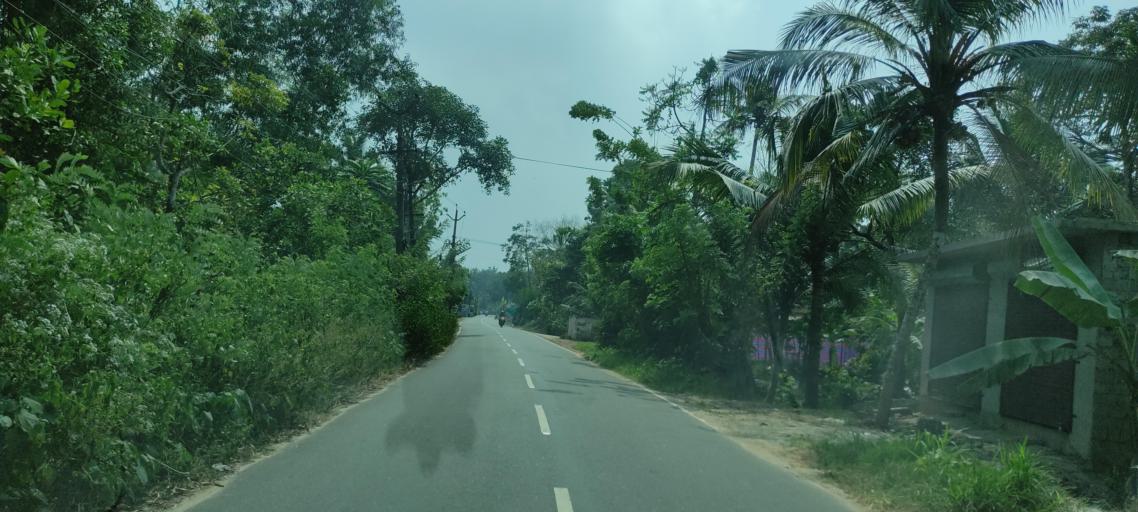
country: IN
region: Kerala
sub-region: Alappuzha
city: Alleppey
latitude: 9.5591
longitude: 76.3339
